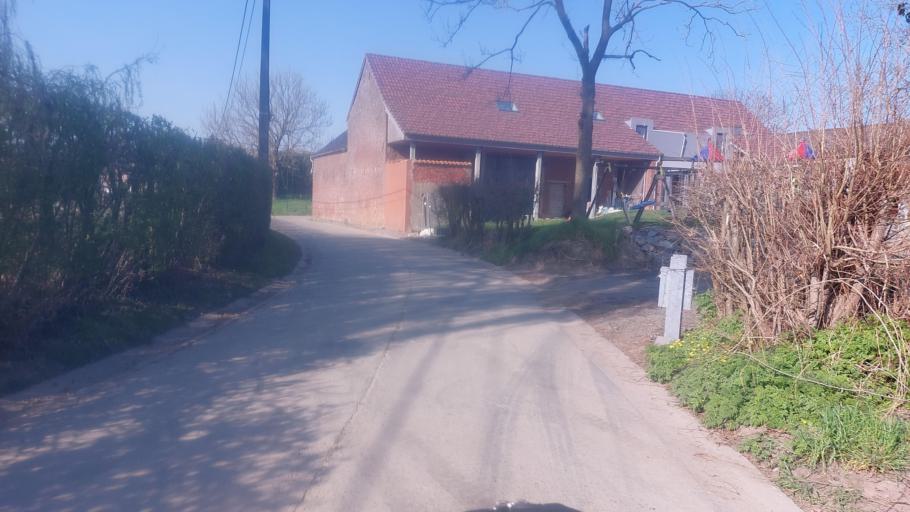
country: BE
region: Wallonia
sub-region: Province du Hainaut
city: Brugelette
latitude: 50.6030
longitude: 3.8867
